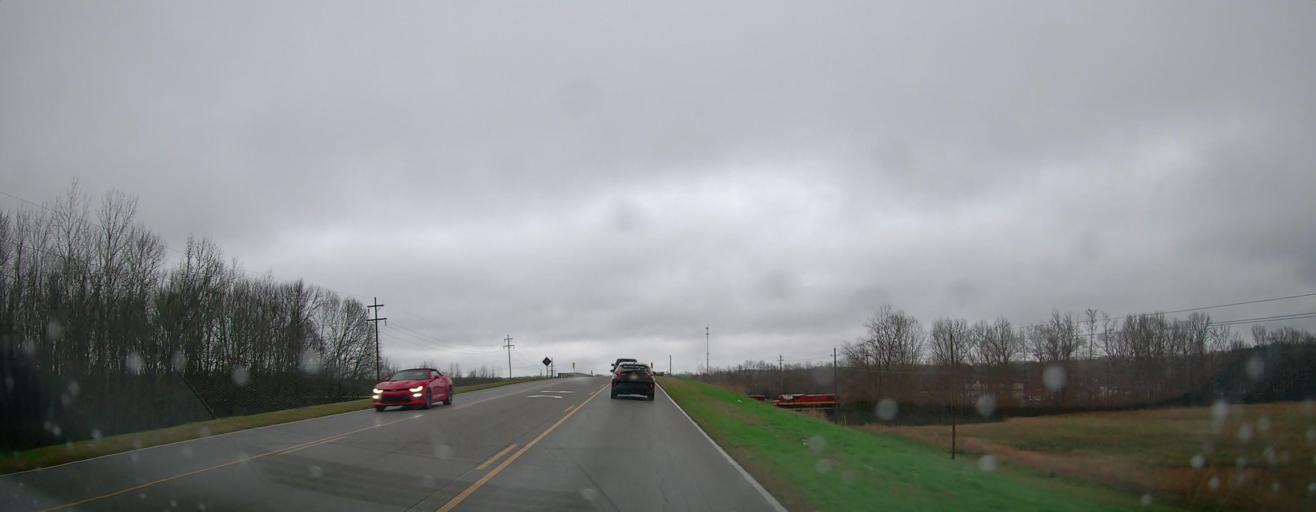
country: US
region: Mississippi
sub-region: Alcorn County
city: Corinth
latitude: 34.9090
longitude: -88.5159
